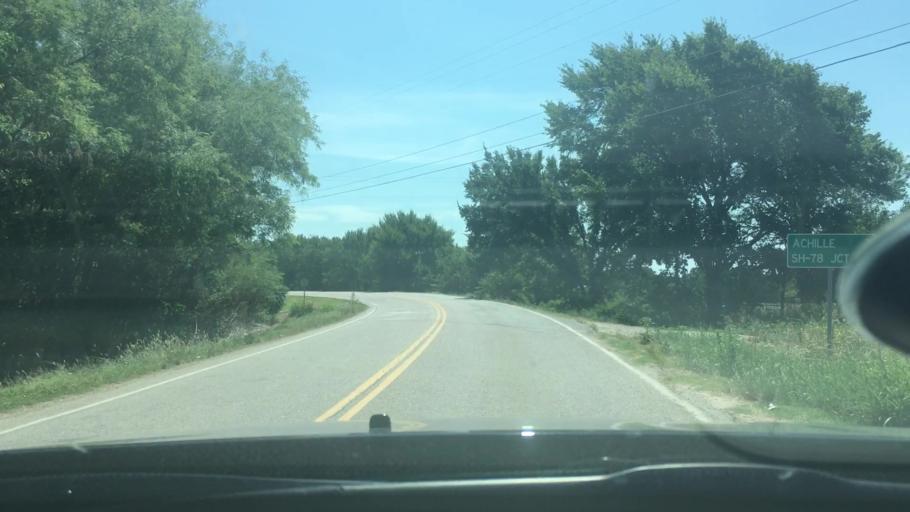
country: US
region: Oklahoma
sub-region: Bryan County
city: Colbert
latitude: 33.8531
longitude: -96.4997
